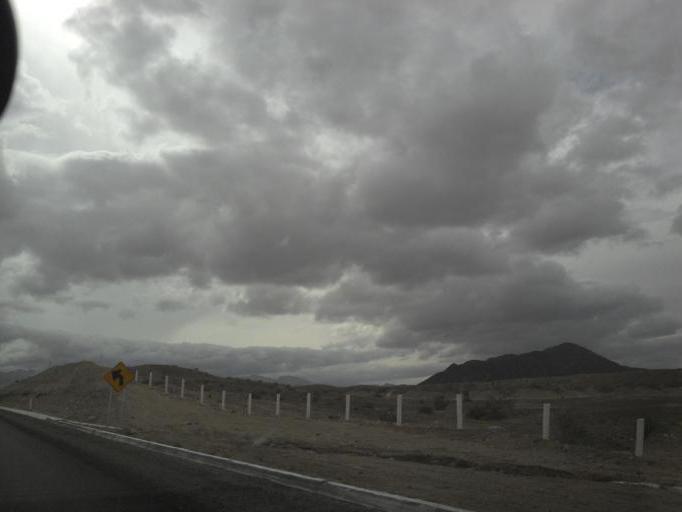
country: MX
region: Baja California
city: Progreso
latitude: 32.5672
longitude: -115.8532
